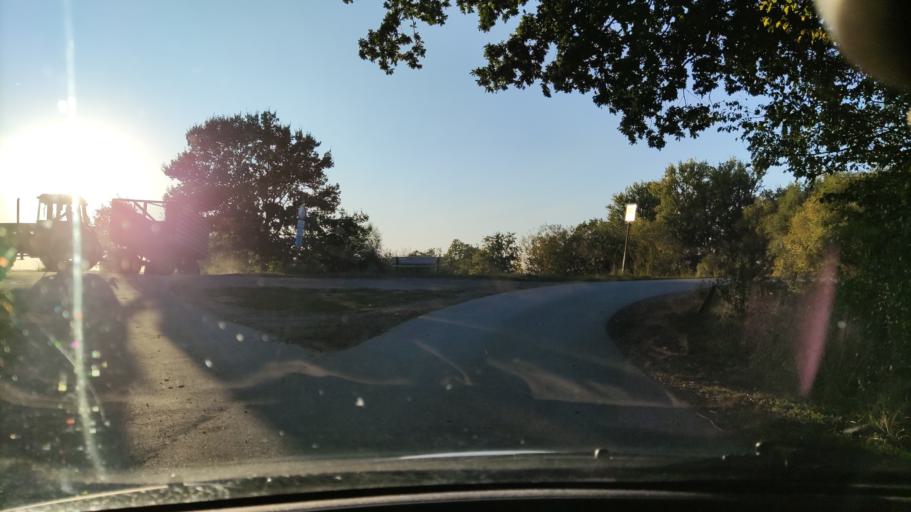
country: DE
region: Lower Saxony
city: Dannenberg
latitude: 53.1218
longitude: 11.0982
